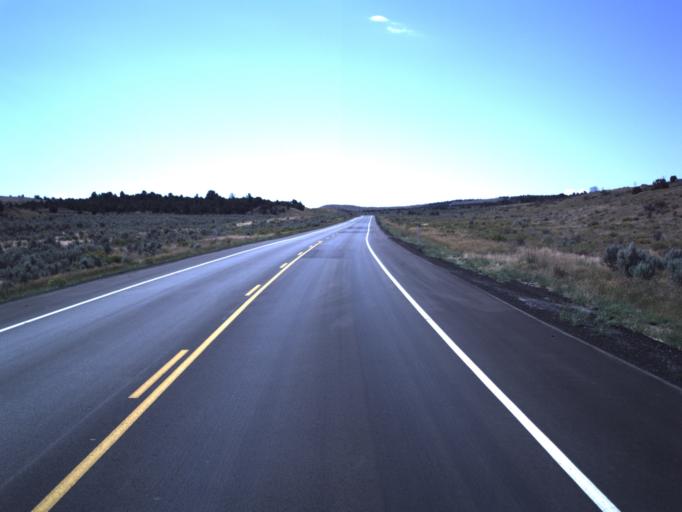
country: US
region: Utah
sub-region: Utah County
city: Eagle Mountain
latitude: 39.9825
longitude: -112.2618
